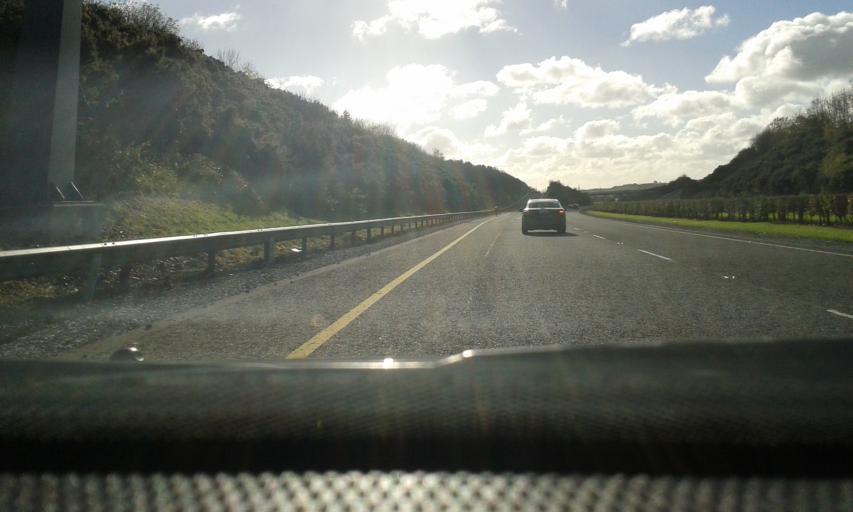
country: IE
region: Munster
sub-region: County Cork
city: Watergrasshill
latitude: 51.9608
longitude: -8.3861
